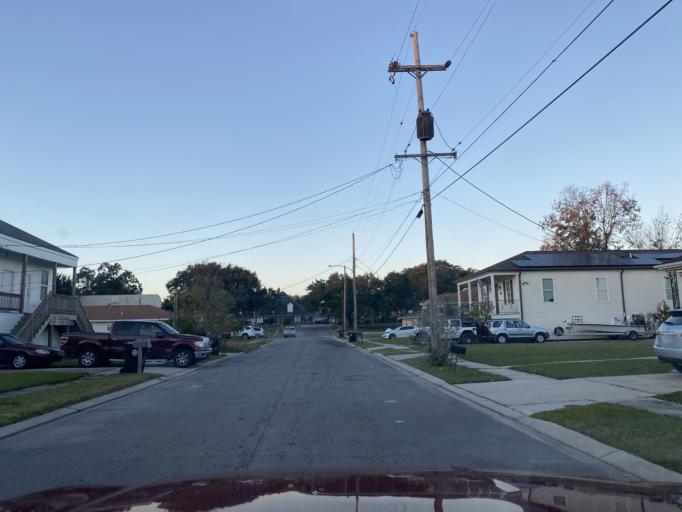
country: US
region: Louisiana
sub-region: Orleans Parish
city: New Orleans
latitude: 30.0246
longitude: -90.0554
